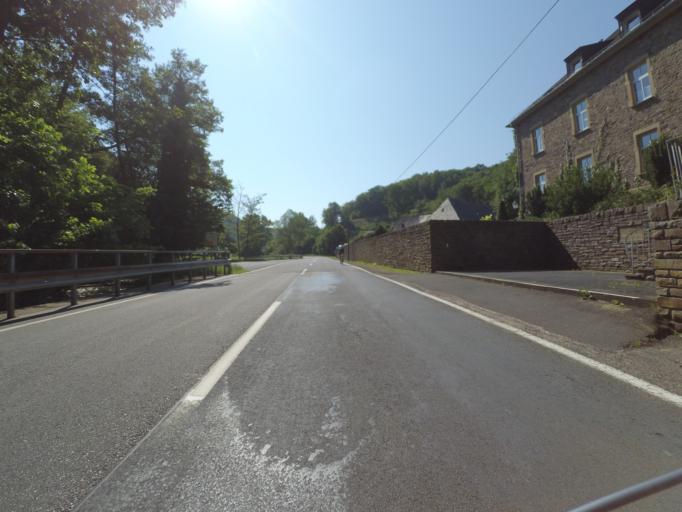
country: DE
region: Rheinland-Pfalz
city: Beilstein
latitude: 50.1256
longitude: 7.2787
